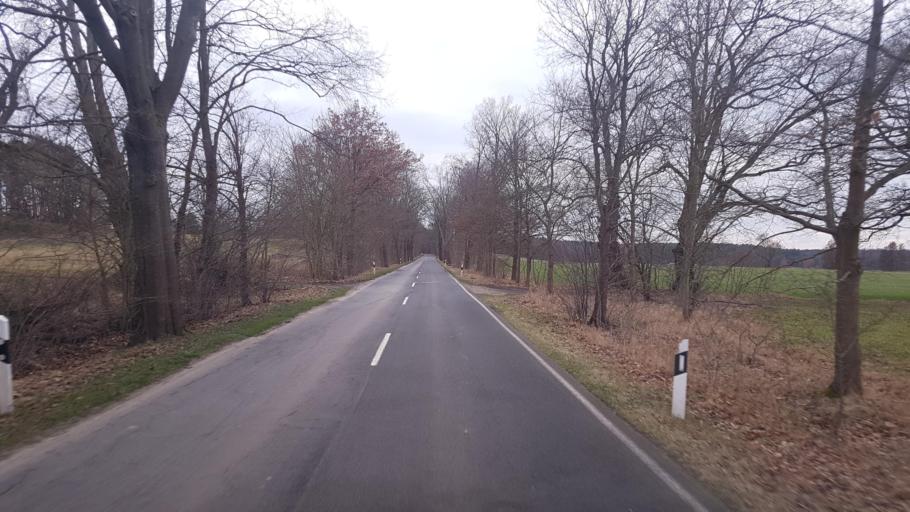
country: DE
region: Brandenburg
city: Halbe
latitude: 52.0806
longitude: 13.7013
